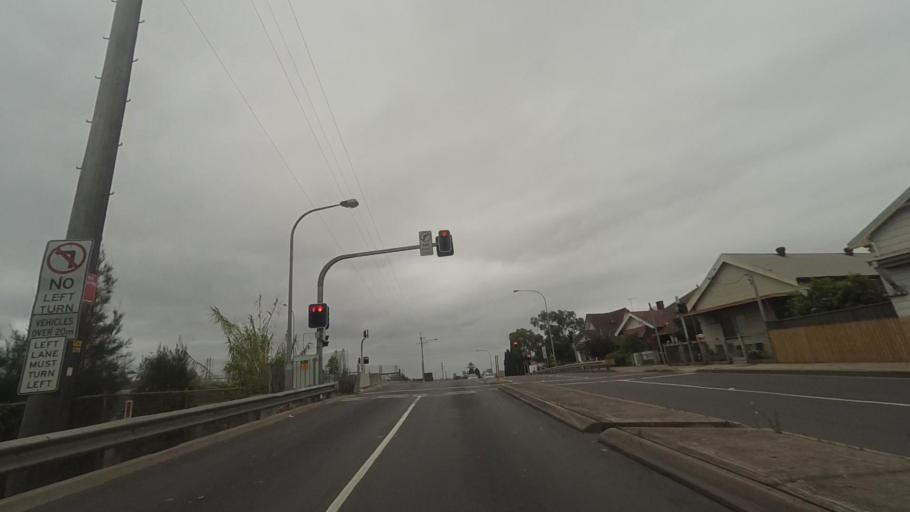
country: AU
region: New South Wales
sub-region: Auburn
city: Auburn
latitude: -33.8474
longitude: 151.0312
